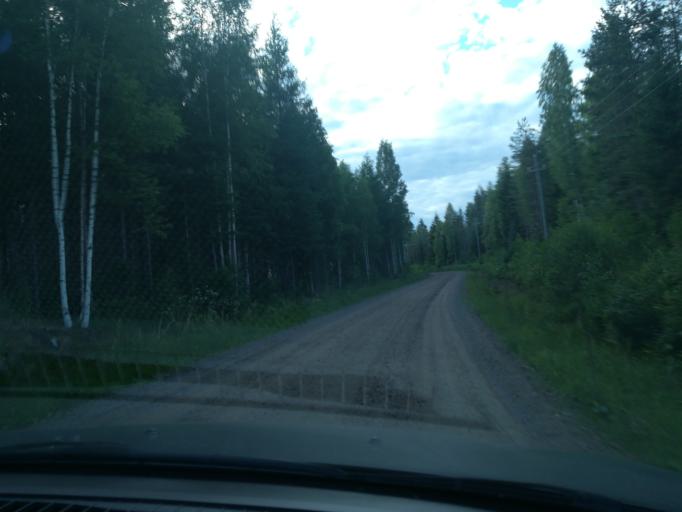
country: FI
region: Southern Savonia
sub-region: Mikkeli
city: Puumala
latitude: 61.6072
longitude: 28.1459
